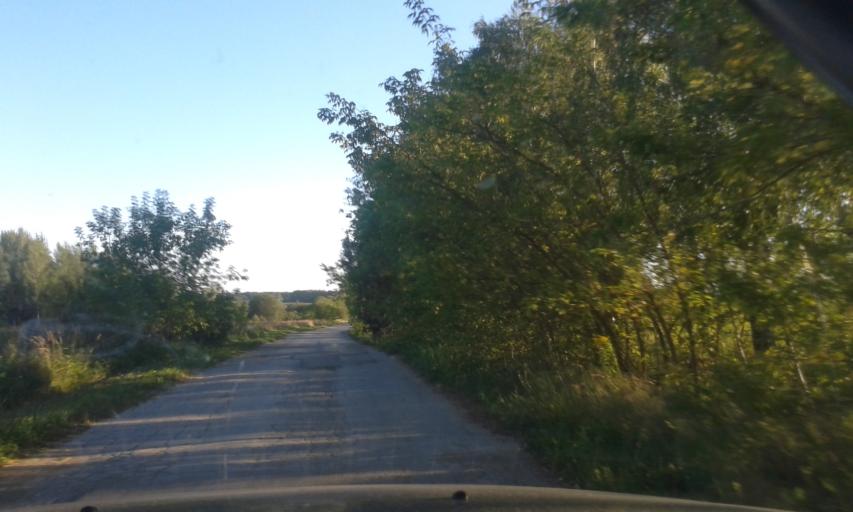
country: RU
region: Tula
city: Krapivna
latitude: 54.1255
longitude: 37.1549
